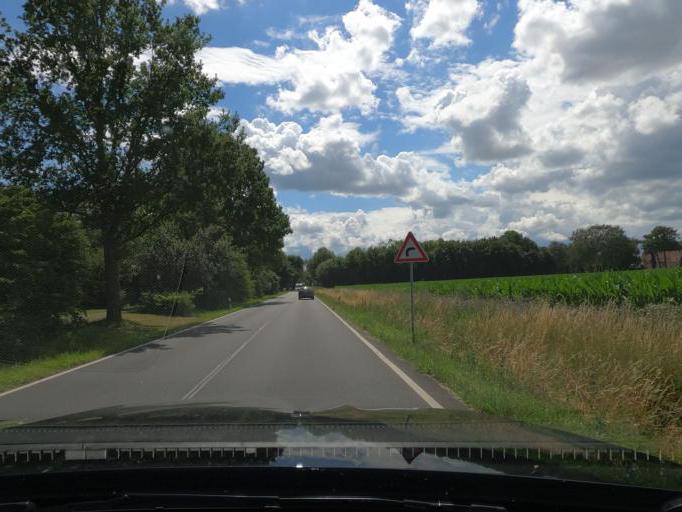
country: DE
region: Lower Saxony
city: Lengede
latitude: 52.1639
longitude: 10.3016
